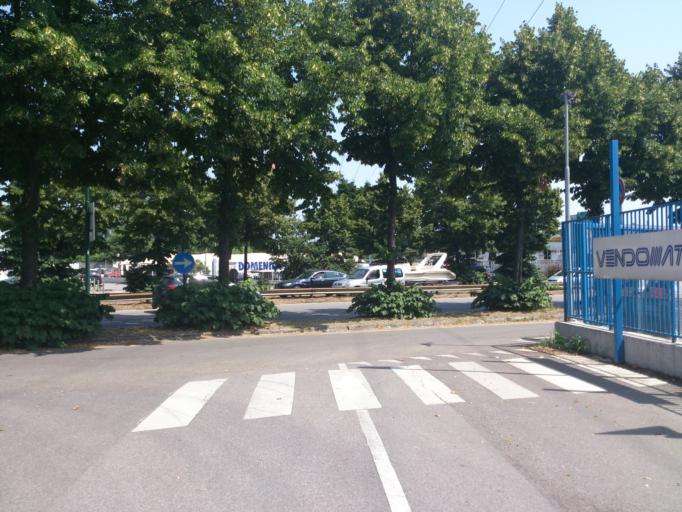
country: IT
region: Lombardy
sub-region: Citta metropolitana di Milano
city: Cologno Monzese
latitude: 45.5275
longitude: 9.2639
